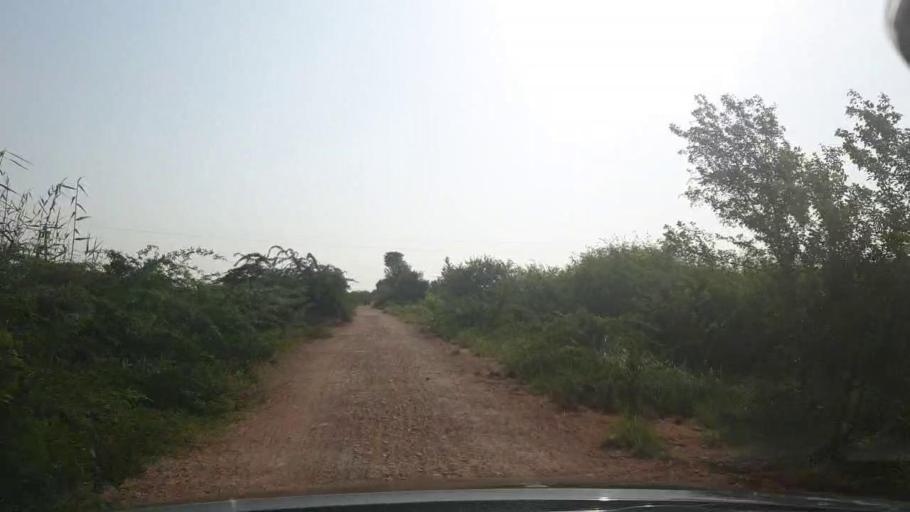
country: PK
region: Sindh
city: Tando Bago
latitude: 24.6509
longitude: 69.1627
